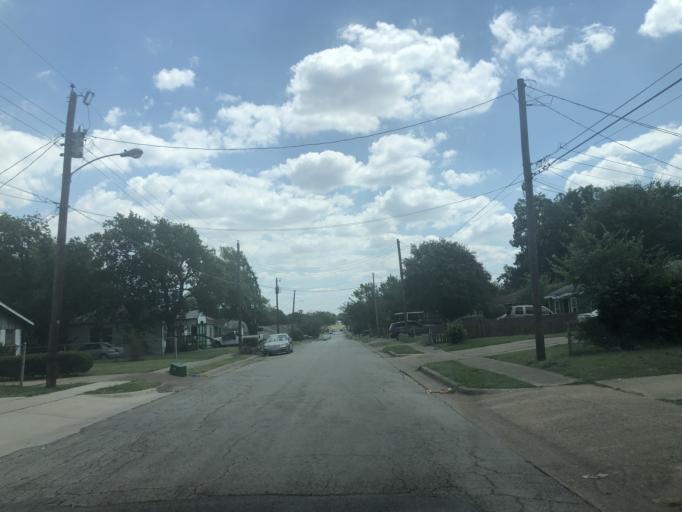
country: US
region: Texas
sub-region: Dallas County
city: Grand Prairie
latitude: 32.7361
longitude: -97.0321
